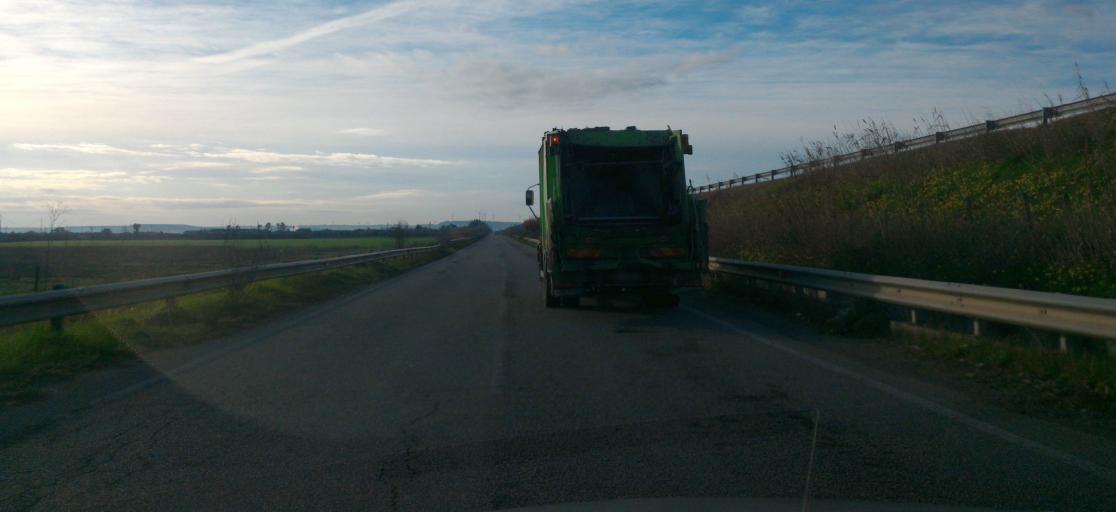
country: IT
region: Calabria
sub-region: Provincia di Crotone
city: Crotone
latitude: 39.1537
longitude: 17.0976
